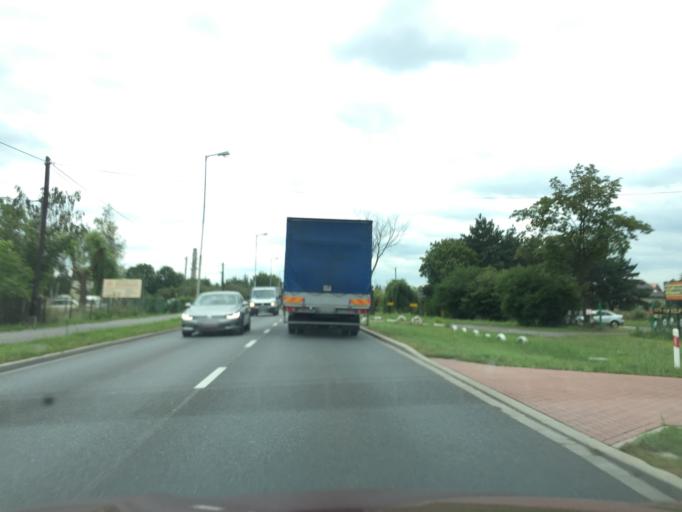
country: PL
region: Greater Poland Voivodeship
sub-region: Kalisz
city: Kalisz
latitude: 51.7878
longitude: 18.0903
